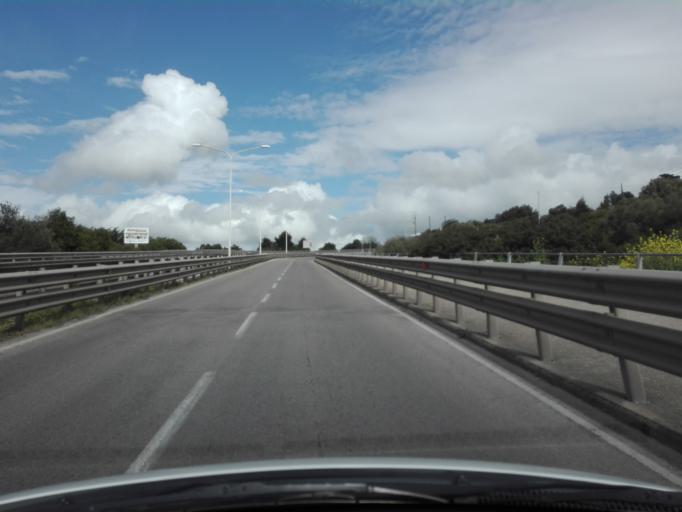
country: IT
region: Sardinia
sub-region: Provincia di Sassari
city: Sassari
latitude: 40.7312
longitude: 8.5741
